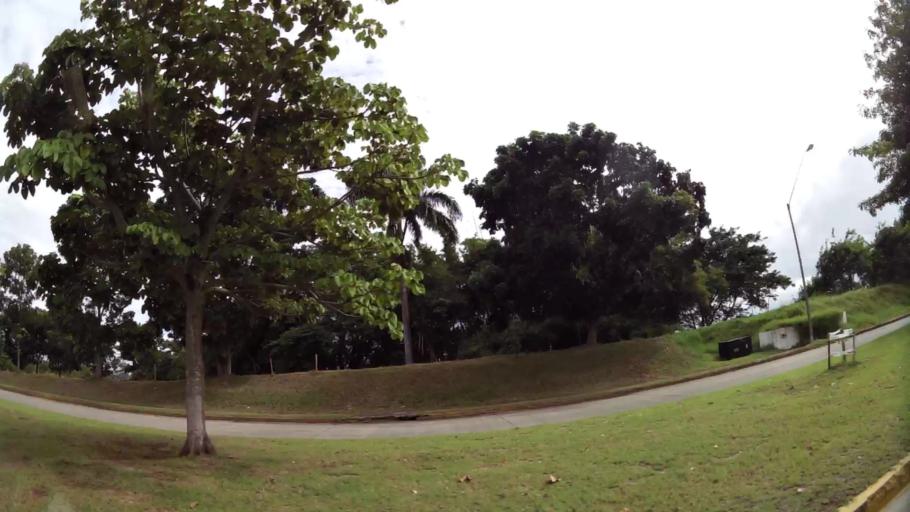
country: PA
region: Panama
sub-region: Distrito de Panama
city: Ancon
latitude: 8.9393
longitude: -79.5452
